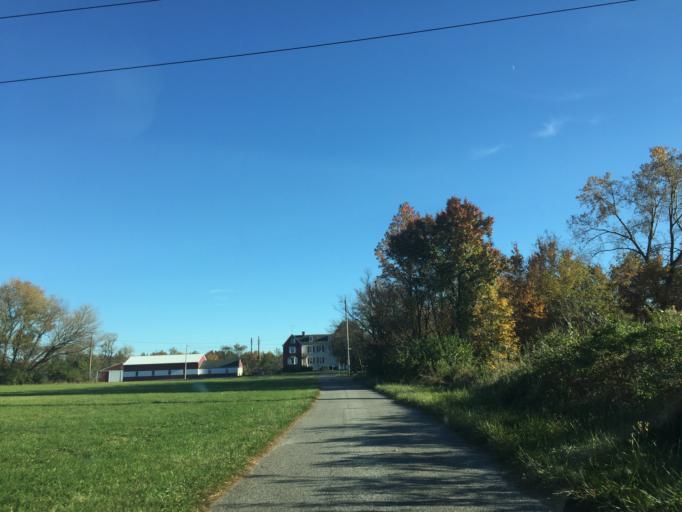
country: US
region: Maryland
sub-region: Baltimore County
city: Essex
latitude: 39.3183
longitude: -76.4939
